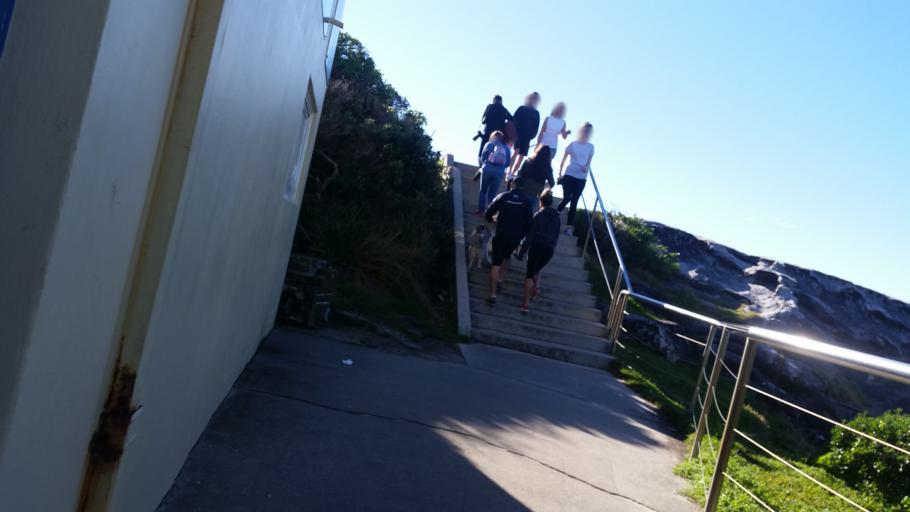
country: AU
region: New South Wales
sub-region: Waverley
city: Bronte
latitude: -33.9001
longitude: 151.2714
